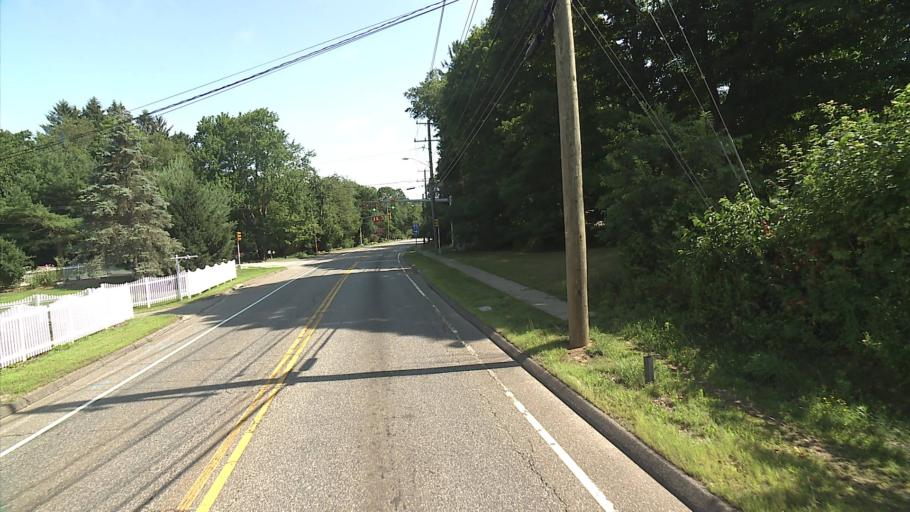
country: US
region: Connecticut
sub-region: Middlesex County
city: Westbrook Center
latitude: 41.2956
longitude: -72.4407
